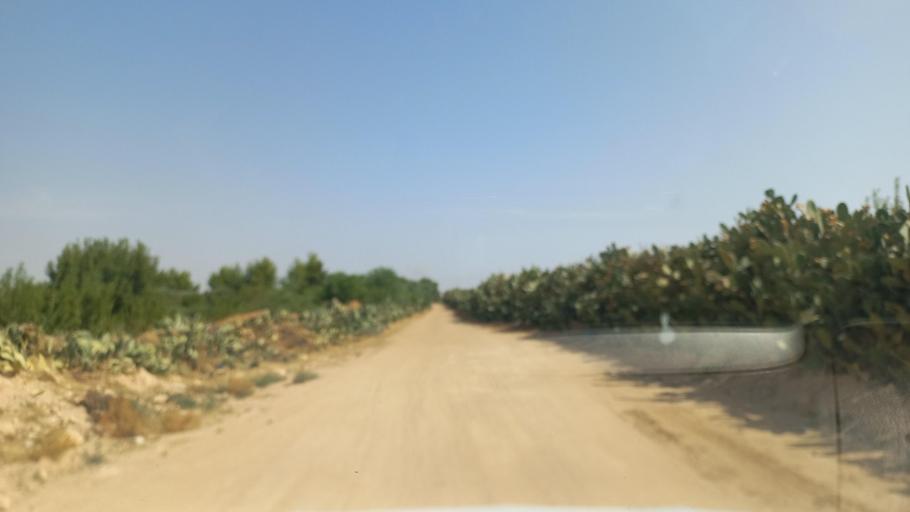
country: TN
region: Al Qasrayn
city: Kasserine
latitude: 35.2386
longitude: 9.0461
